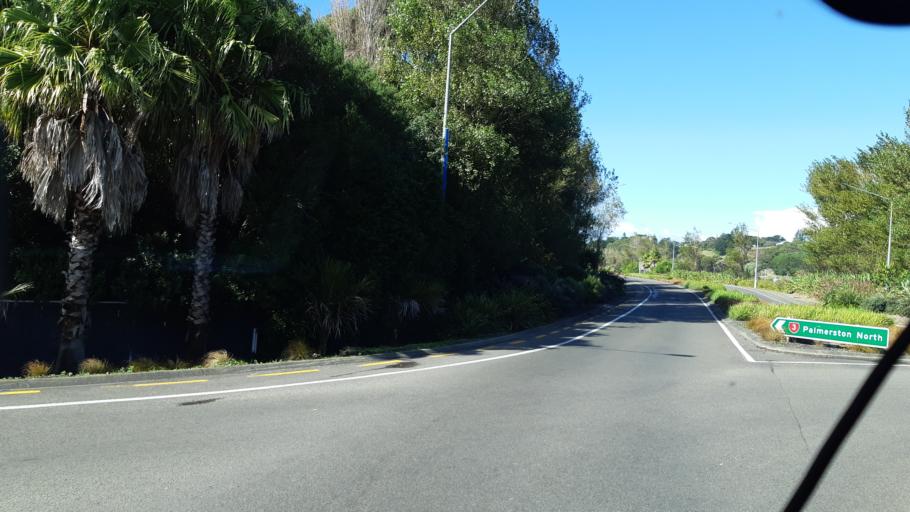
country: NZ
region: Manawatu-Wanganui
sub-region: Wanganui District
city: Wanganui
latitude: -39.9484
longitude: 175.0510
